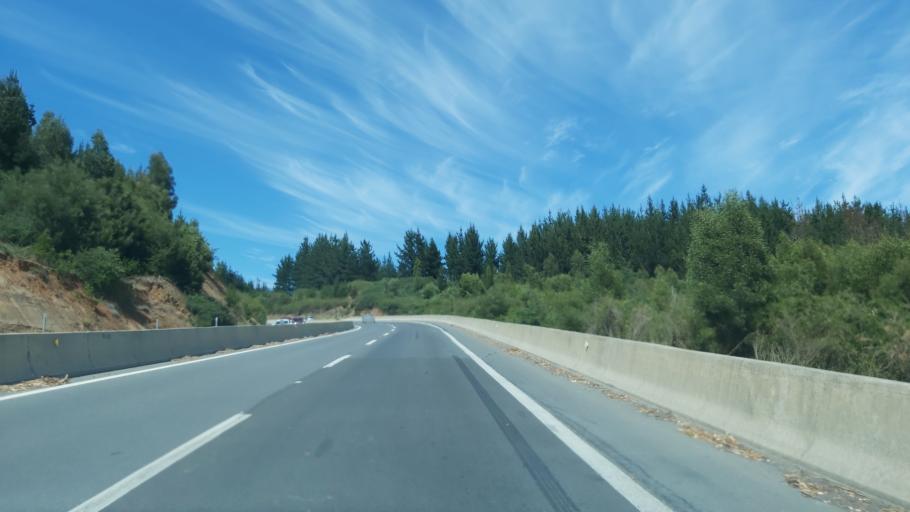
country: CL
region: Biobio
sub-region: Provincia de Concepcion
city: Lota
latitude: -37.0756
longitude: -73.1371
